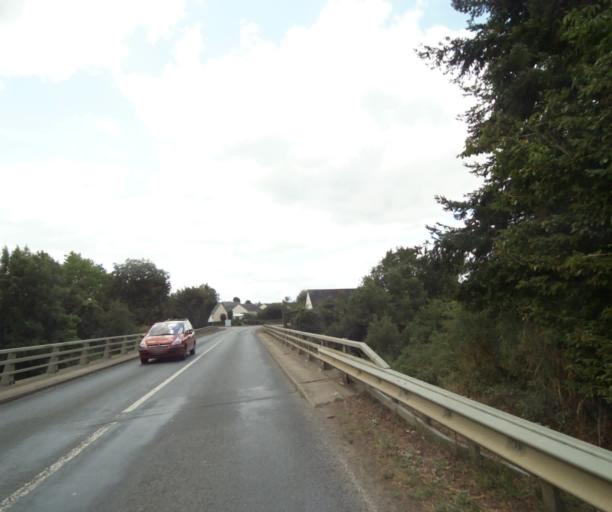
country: FR
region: Pays de la Loire
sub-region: Departement de la Sarthe
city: Sable-sur-Sarthe
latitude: 47.8484
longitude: -0.3287
